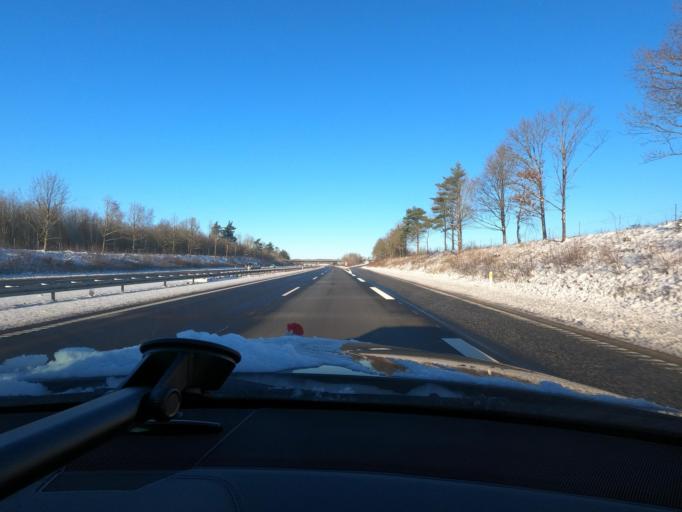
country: DK
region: South Denmark
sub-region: Aabenraa Kommune
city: Aabenraa
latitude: 54.9793
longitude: 9.3810
